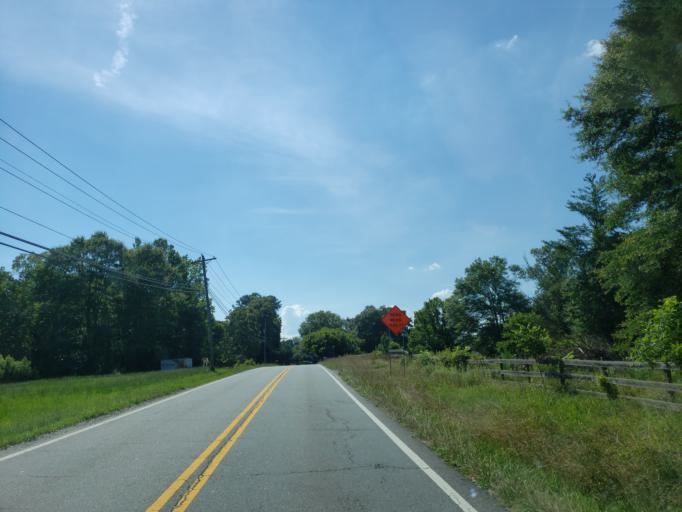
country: US
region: Georgia
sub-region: Cherokee County
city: Woodstock
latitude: 34.1106
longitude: -84.4521
